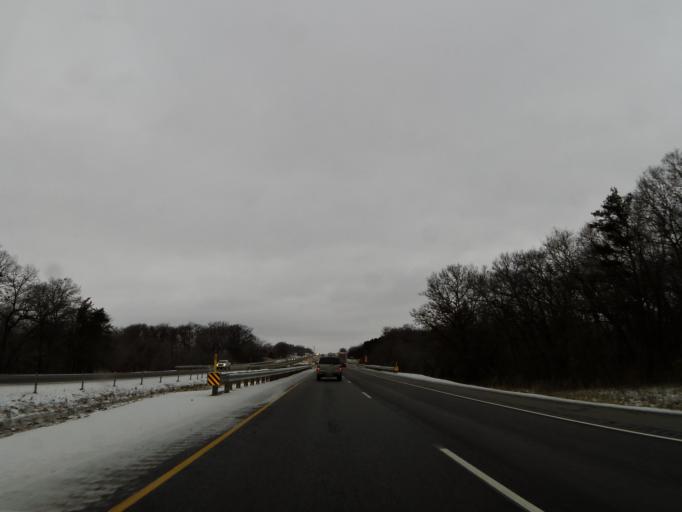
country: US
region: Wisconsin
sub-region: Eau Claire County
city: Eau Claire
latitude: 44.8533
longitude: -91.6477
